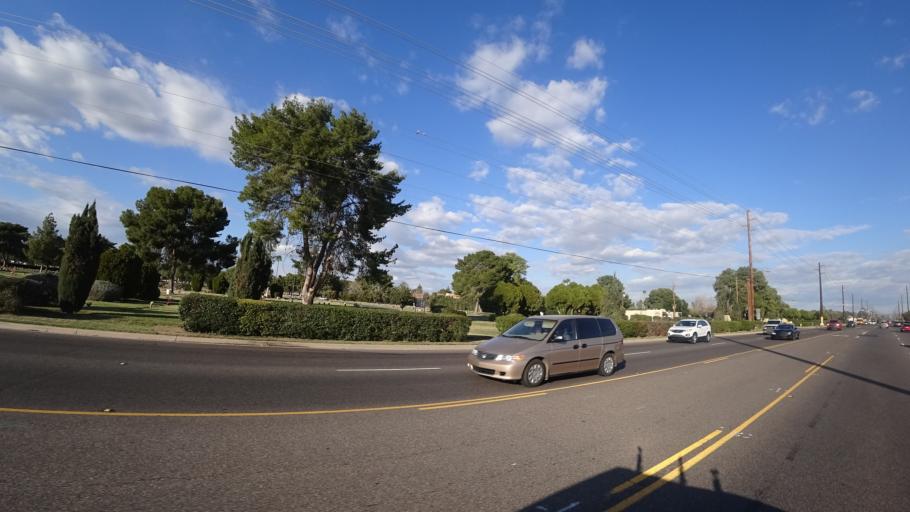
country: US
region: Arizona
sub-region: Maricopa County
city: Glendale
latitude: 33.5528
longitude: -112.1961
